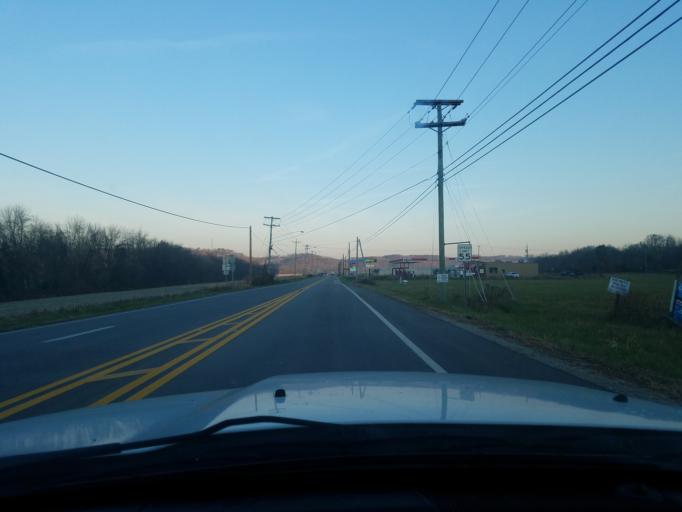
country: US
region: West Virginia
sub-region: Putnam County
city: Buffalo
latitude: 38.5843
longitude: -81.9945
